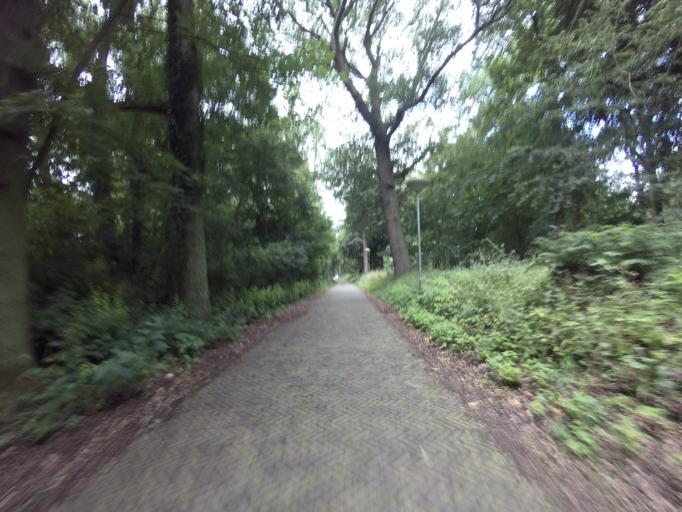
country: NL
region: North Holland
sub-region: Gemeente Velsen
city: Velsen-Zuid
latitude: 52.4566
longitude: 4.6416
